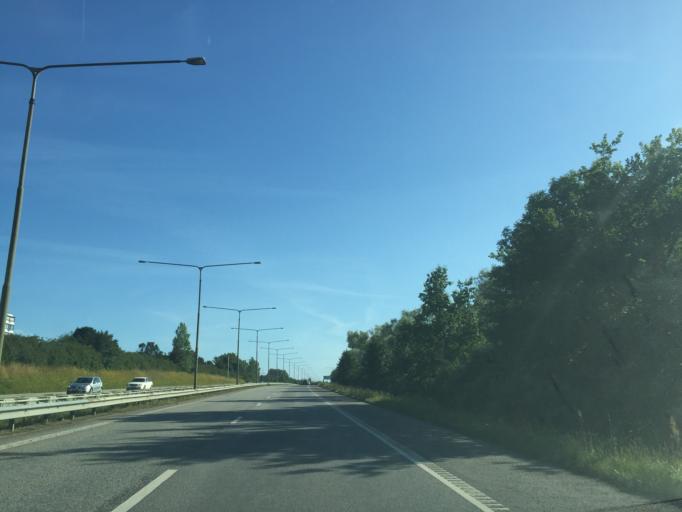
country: SE
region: Skane
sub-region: Malmo
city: Malmoe
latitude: 55.5710
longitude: 13.0041
